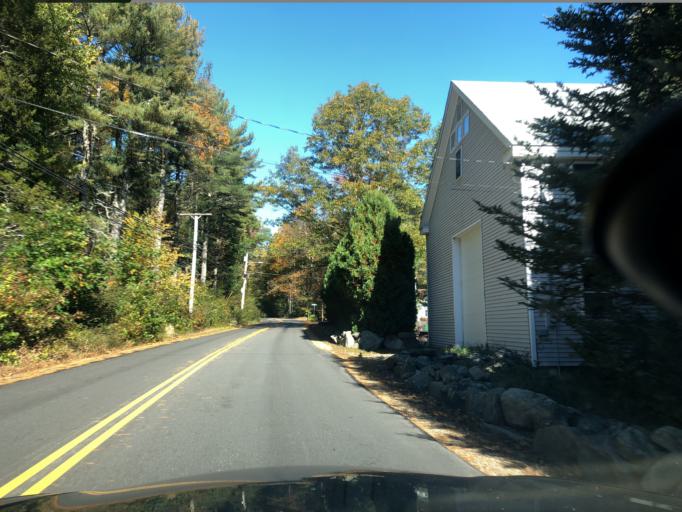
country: US
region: New Hampshire
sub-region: Rockingham County
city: Newmarket
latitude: 43.0896
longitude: -70.9476
